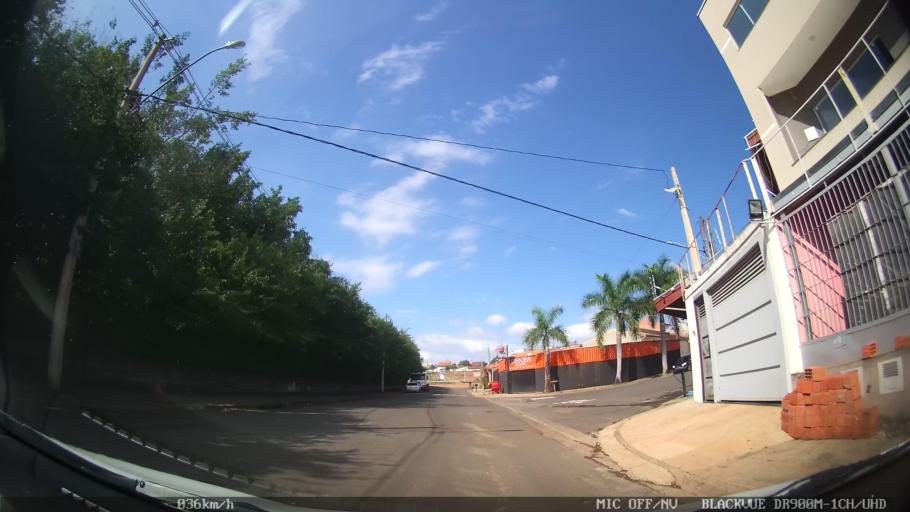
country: BR
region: Sao Paulo
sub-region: Americana
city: Americana
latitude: -22.7152
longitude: -47.3179
